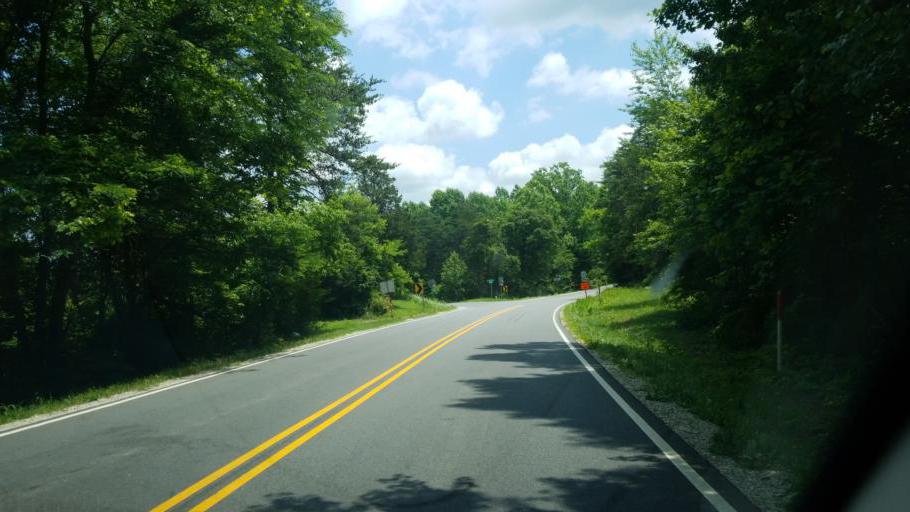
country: US
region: Virginia
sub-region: Nelson County
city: Lovingston
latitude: 37.5768
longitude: -78.8664
